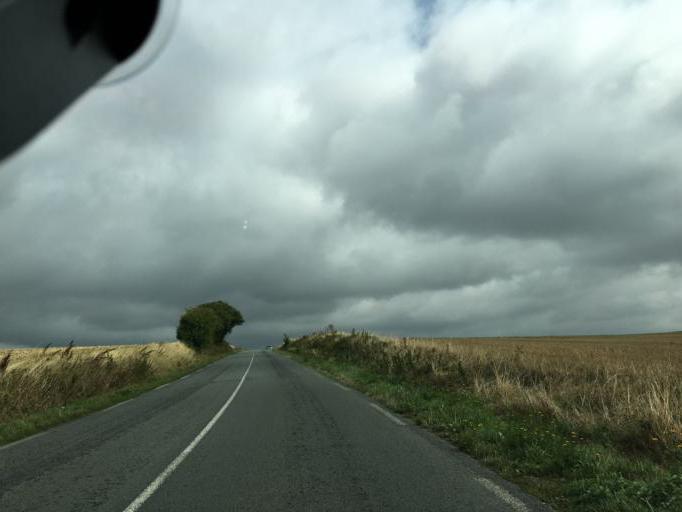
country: FR
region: Nord-Pas-de-Calais
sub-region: Departement du Pas-de-Calais
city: Rang-du-Fliers
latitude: 50.4245
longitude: 1.6870
